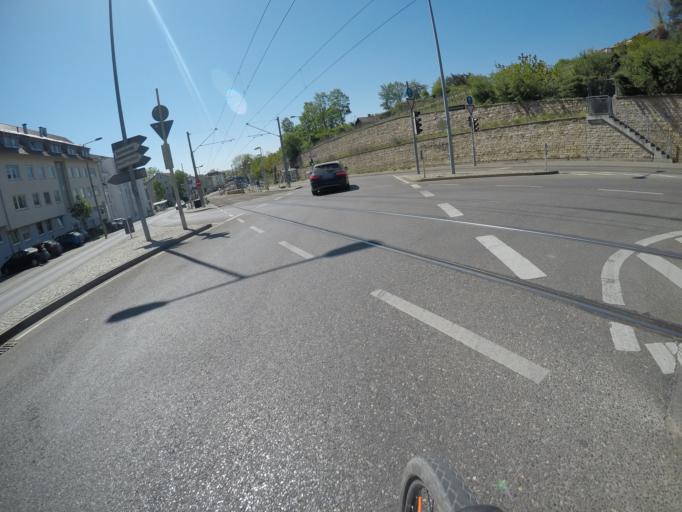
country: DE
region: Baden-Wuerttemberg
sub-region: Regierungsbezirk Stuttgart
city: Stuttgart Muehlhausen
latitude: 48.8156
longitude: 9.2361
